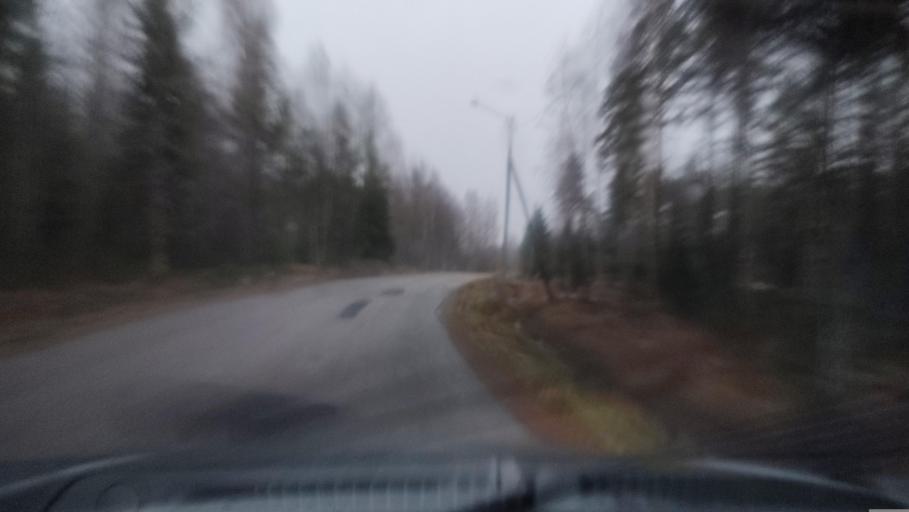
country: FI
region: Southern Ostrobothnia
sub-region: Suupohja
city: Karijoki
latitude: 62.1415
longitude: 21.5718
